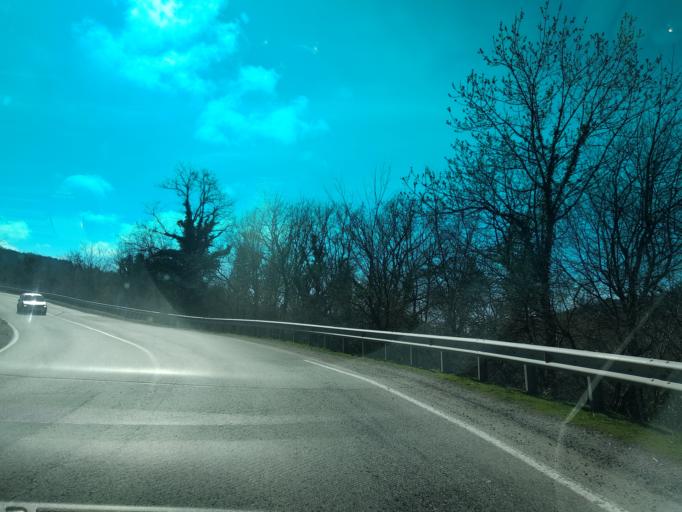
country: RU
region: Krasnodarskiy
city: Tuapse
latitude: 44.0906
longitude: 39.1184
